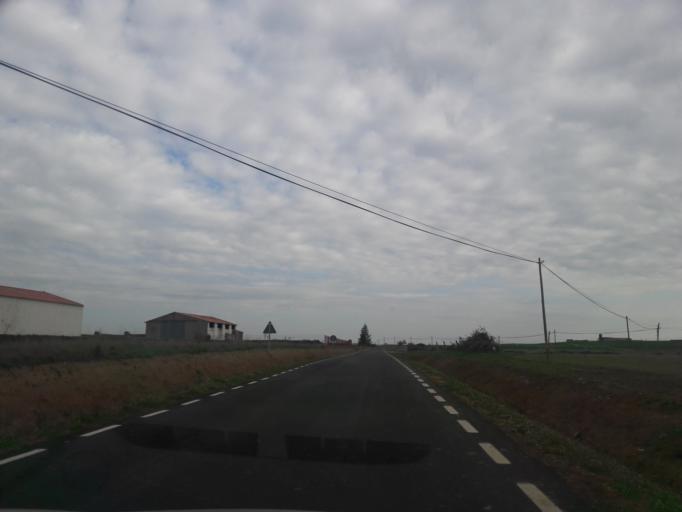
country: ES
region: Castille and Leon
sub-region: Provincia de Salamanca
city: Pastores
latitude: 40.5019
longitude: -6.5307
